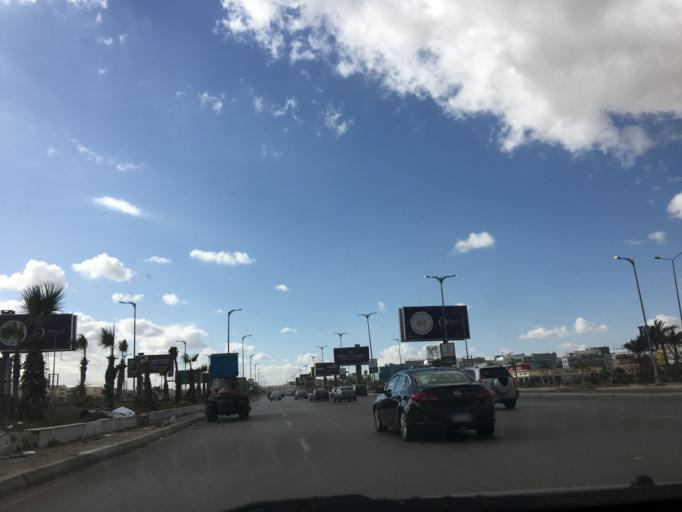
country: EG
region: Al Jizah
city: Awsim
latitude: 30.0276
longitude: 31.0202
